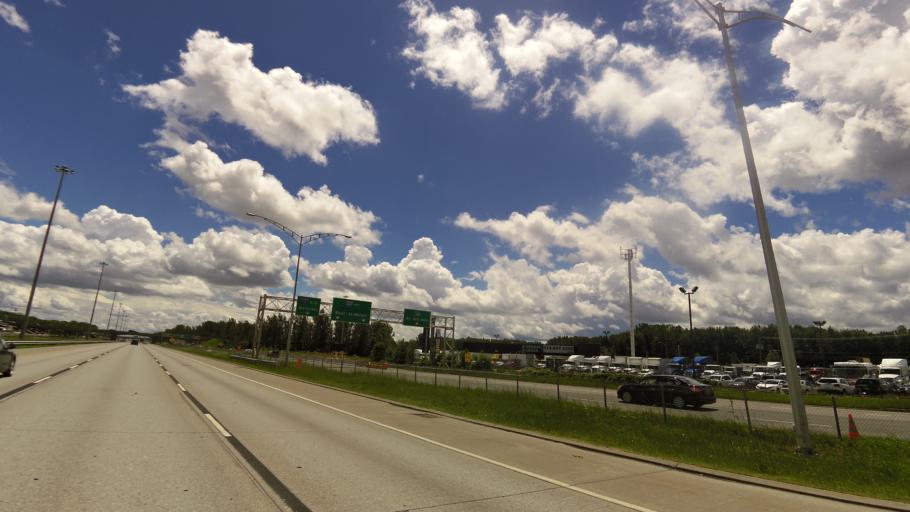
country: CA
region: Quebec
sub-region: Laurentides
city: Boisbriand
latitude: 45.5578
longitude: -73.8129
